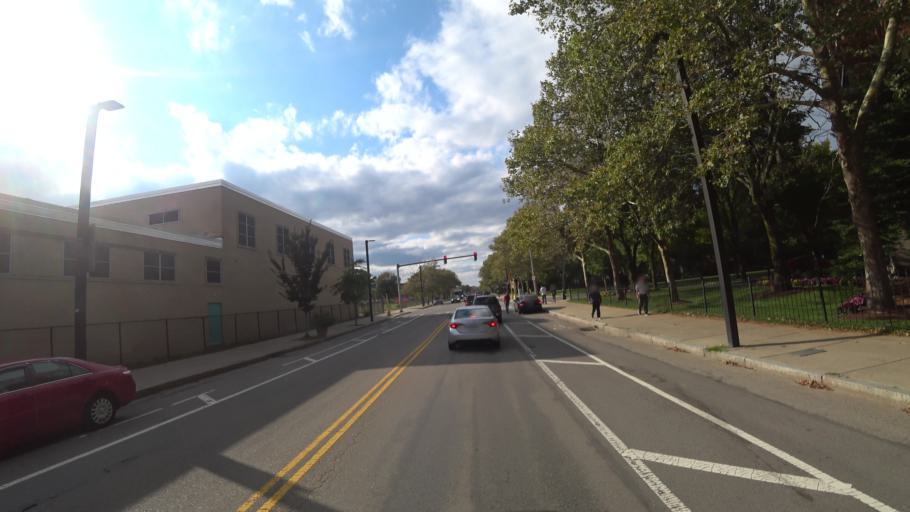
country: US
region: Massachusetts
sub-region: Suffolk County
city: South Boston
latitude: 42.3183
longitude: -71.0435
